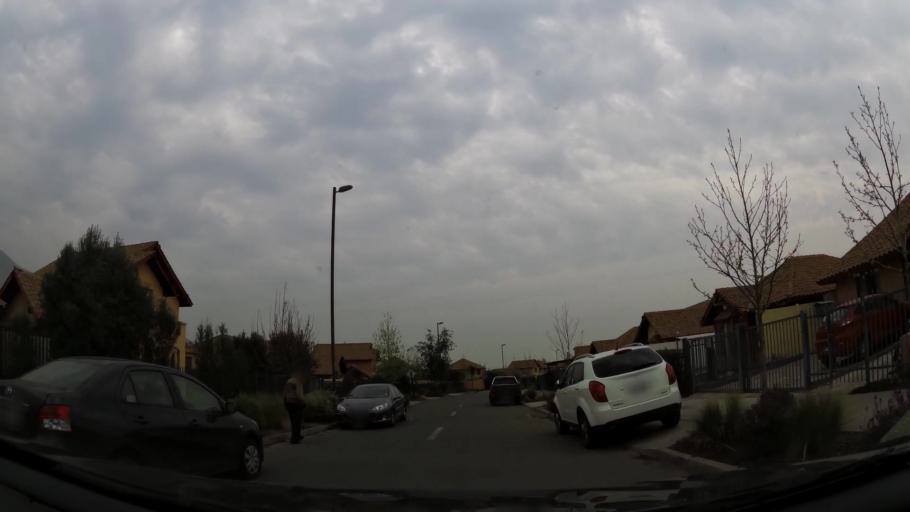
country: CL
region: Santiago Metropolitan
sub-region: Provincia de Chacabuco
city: Chicureo Abajo
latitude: -33.1993
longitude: -70.6513
